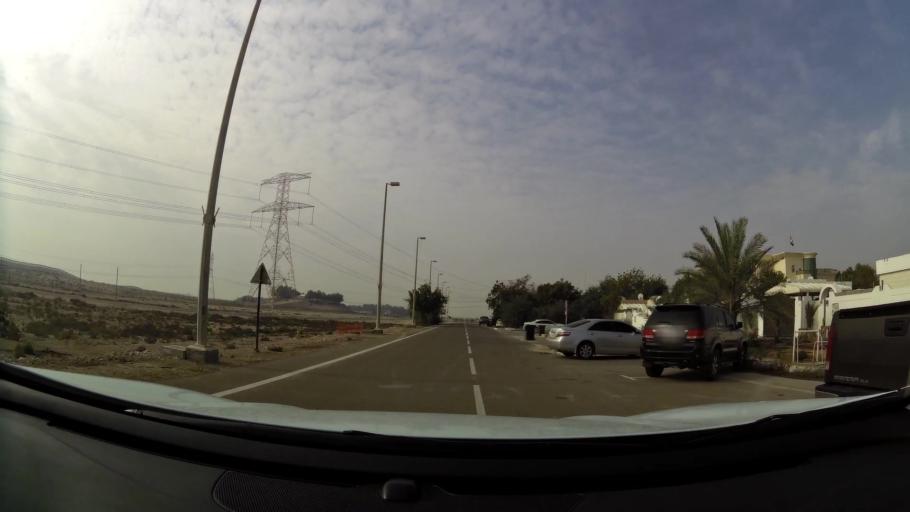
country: AE
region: Abu Dhabi
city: Abu Dhabi
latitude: 24.6549
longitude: 54.7650
